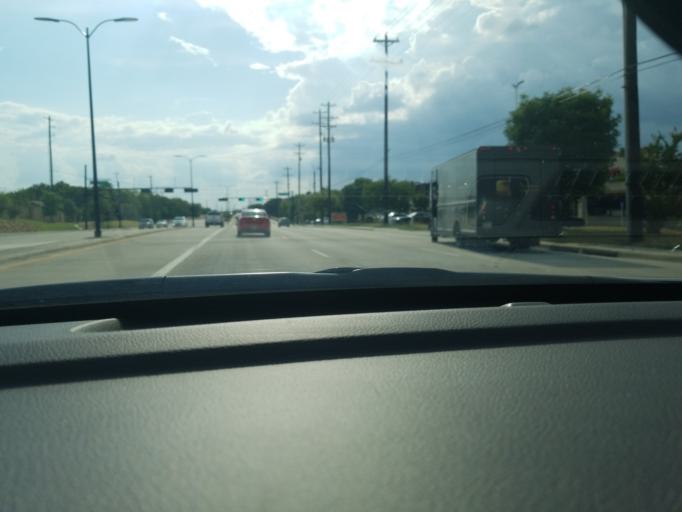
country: US
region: Texas
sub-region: Denton County
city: Little Elm
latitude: 33.1686
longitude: -96.9067
